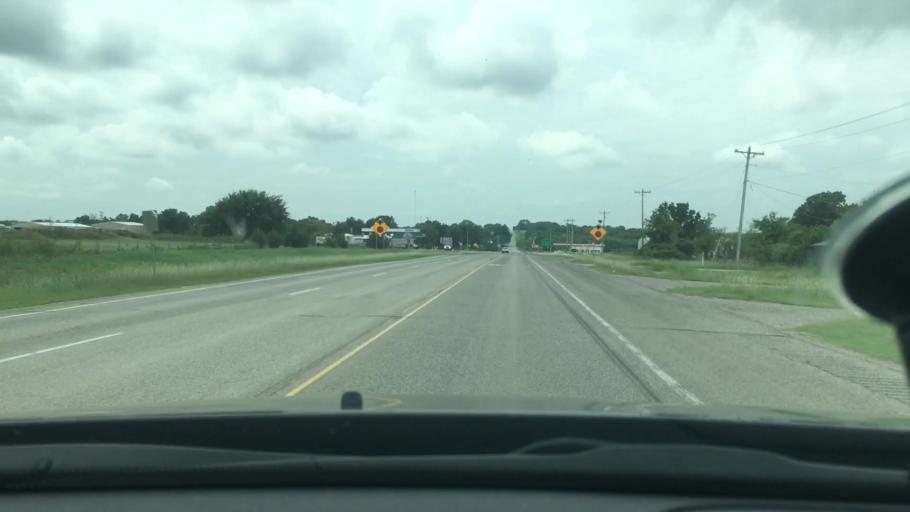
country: US
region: Oklahoma
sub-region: Carter County
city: Wilson
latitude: 34.1765
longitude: -97.4749
